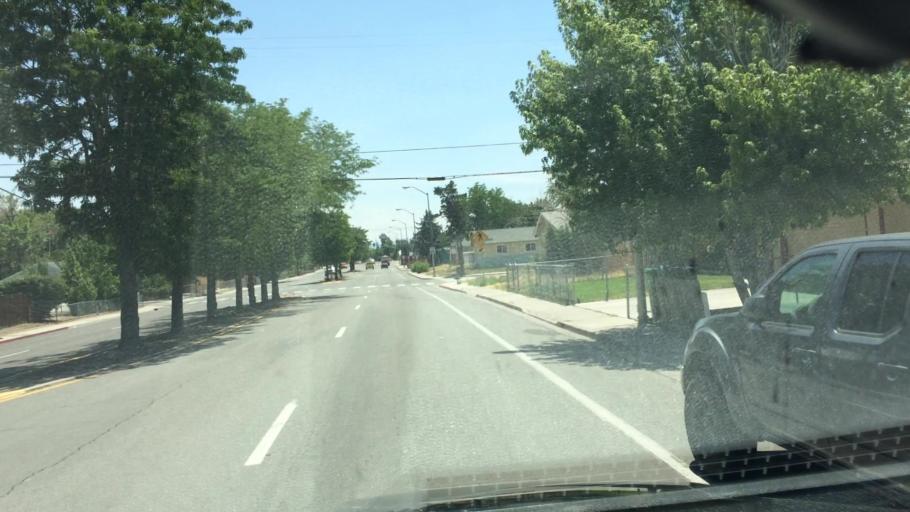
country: US
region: Nevada
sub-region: Washoe County
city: Sparks
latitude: 39.5481
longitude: -119.7621
